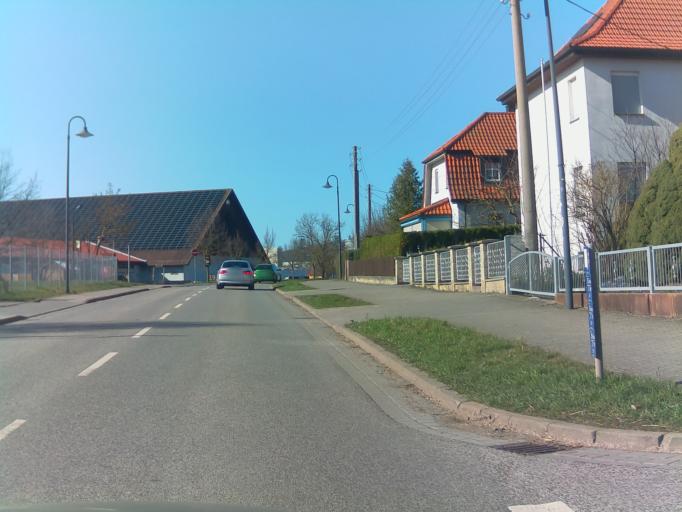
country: DE
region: Thuringia
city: Romhild
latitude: 50.4022
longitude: 10.5403
